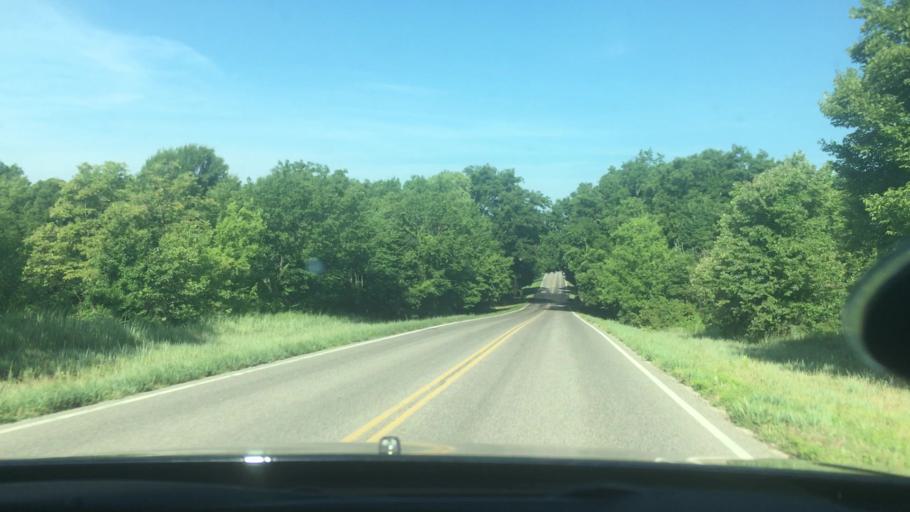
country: US
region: Oklahoma
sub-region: Garvin County
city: Pauls Valley
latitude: 34.6520
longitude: -97.3047
